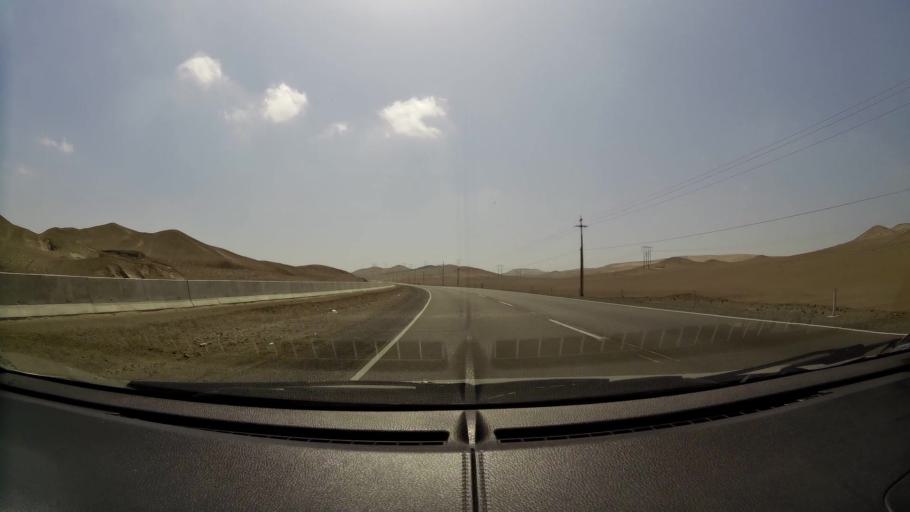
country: PE
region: Ancash
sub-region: Provincia de Huarmey
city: Huarmey
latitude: -10.2020
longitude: -78.0504
